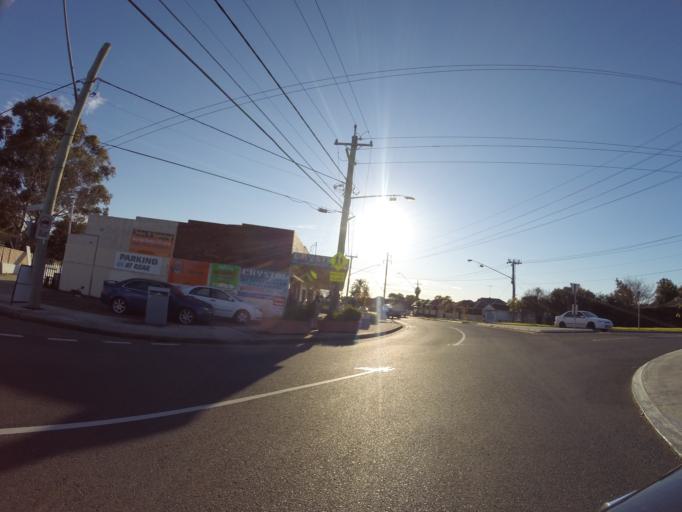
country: AU
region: New South Wales
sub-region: Fairfield
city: Fairfield Heights
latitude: -33.8571
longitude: 150.9504
